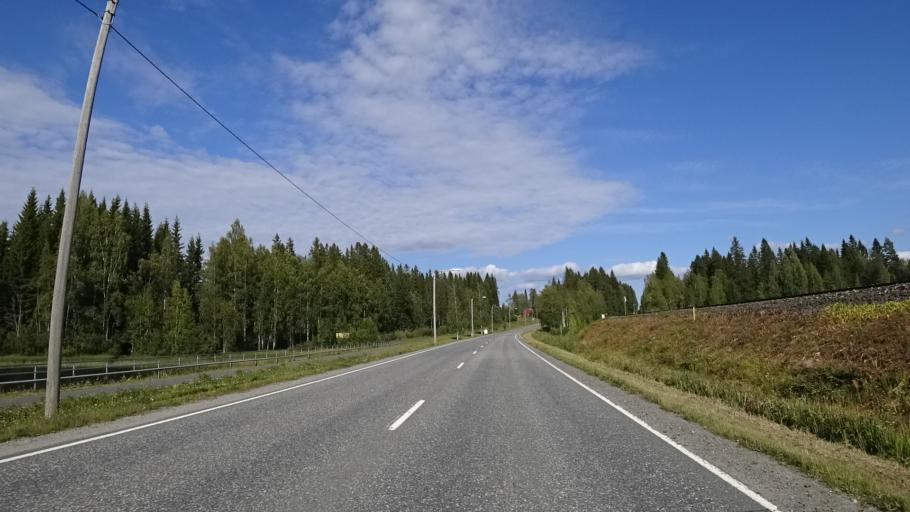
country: FI
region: North Karelia
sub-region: Joensuu
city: Eno
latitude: 62.8037
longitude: 30.1235
